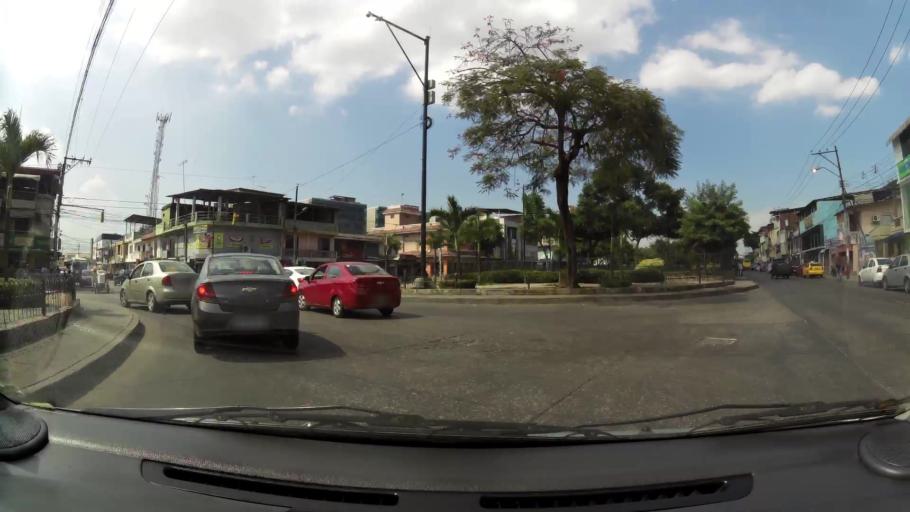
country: EC
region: Guayas
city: Guayaquil
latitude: -2.1291
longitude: -79.9362
